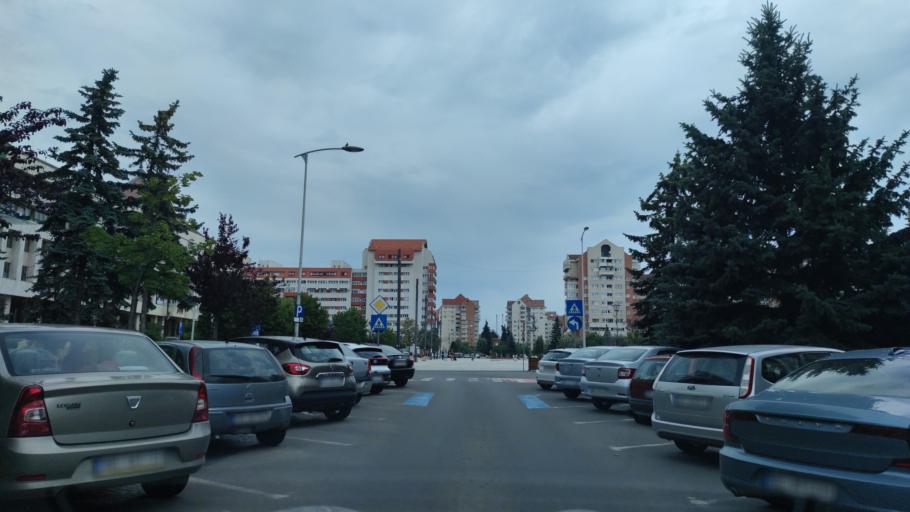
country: RO
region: Harghita
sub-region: Municipiul Miercurea Ciuc
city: Miercurea-Ciuc
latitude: 46.3604
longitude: 25.8025
